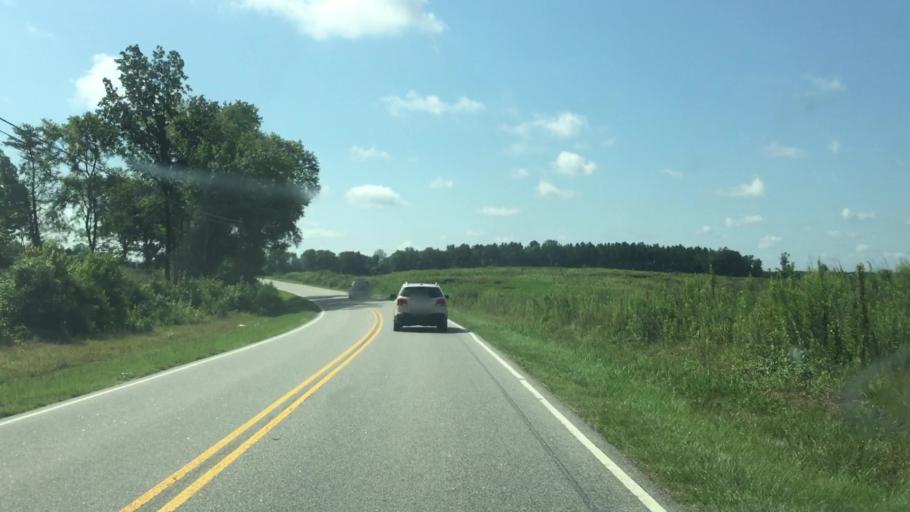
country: US
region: North Carolina
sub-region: Anson County
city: Polkton
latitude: 35.0145
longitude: -80.2187
